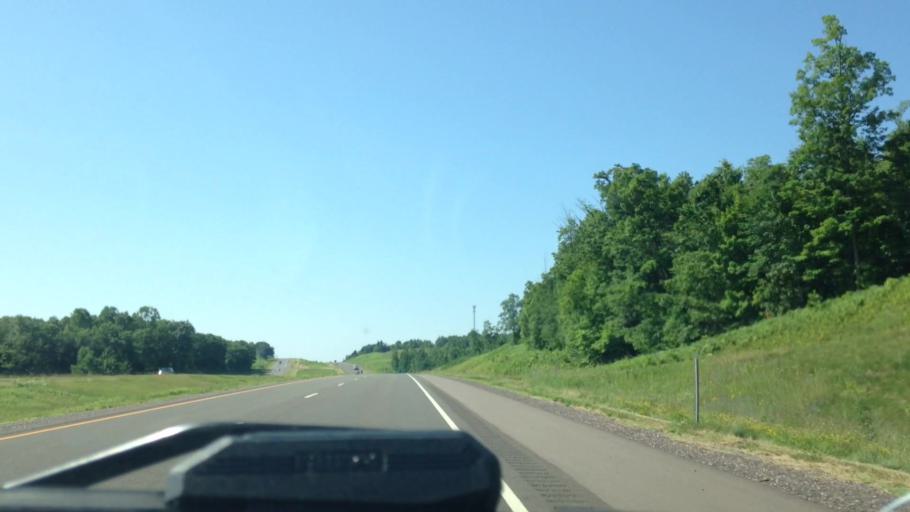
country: US
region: Wisconsin
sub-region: Washburn County
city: Spooner
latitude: 45.9700
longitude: -91.8280
